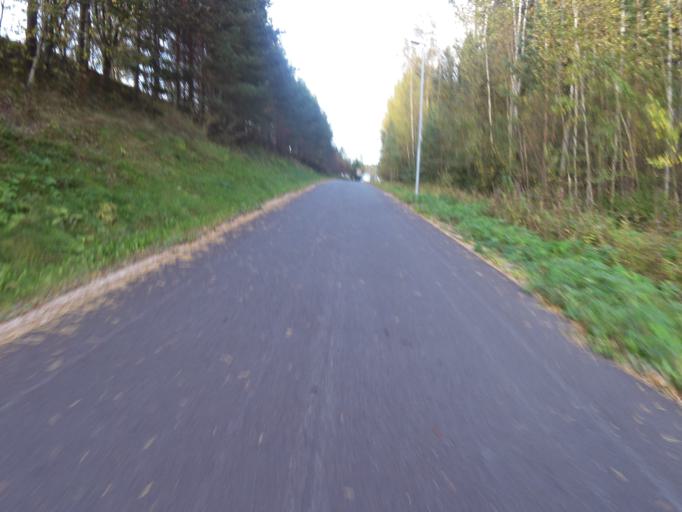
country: FI
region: Uusimaa
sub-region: Helsinki
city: Kauniainen
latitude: 60.2576
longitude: 24.7213
